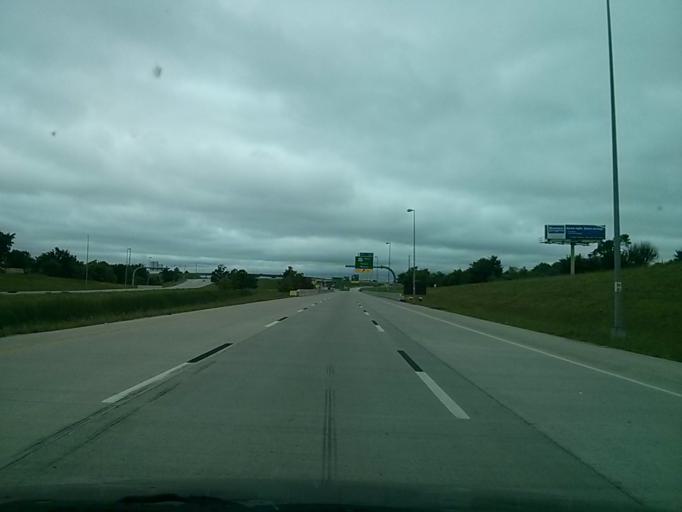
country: US
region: Oklahoma
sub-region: Tulsa County
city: Owasso
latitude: 36.1663
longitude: -95.8519
